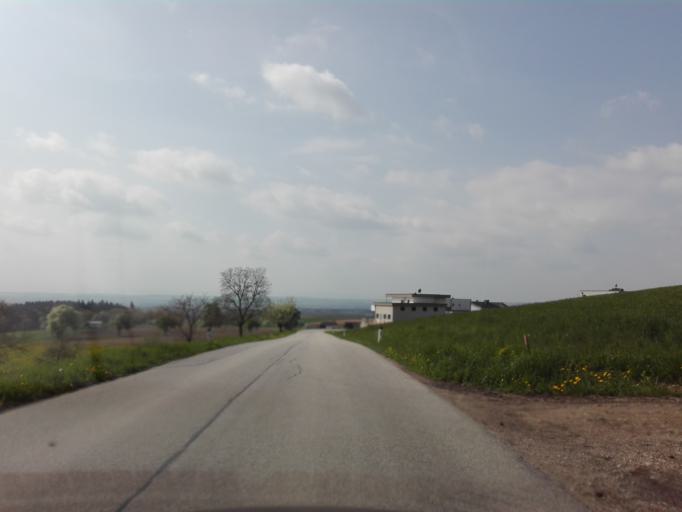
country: AT
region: Upper Austria
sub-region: Politischer Bezirk Perg
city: Perg
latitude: 48.2445
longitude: 14.7012
